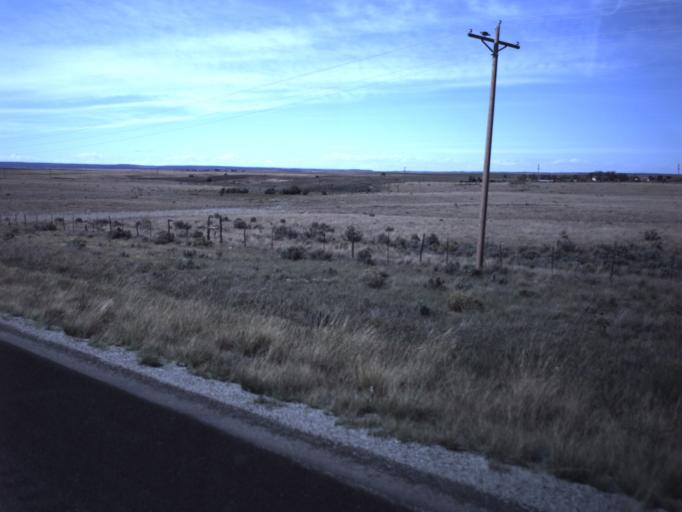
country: US
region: Utah
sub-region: San Juan County
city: Monticello
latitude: 37.8668
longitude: -109.2372
